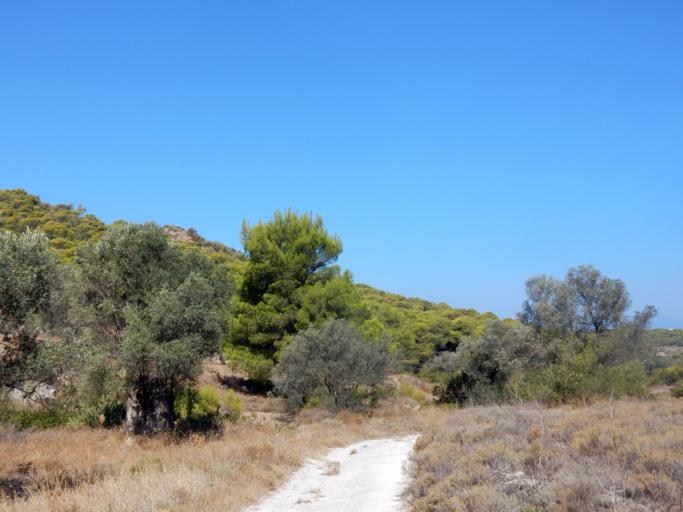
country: GR
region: Attica
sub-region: Nomos Piraios
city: Vathi
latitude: 37.7620
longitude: 23.5393
